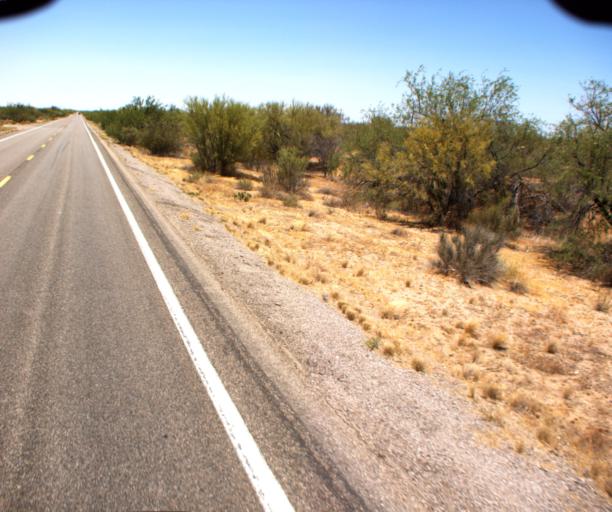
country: US
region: Arizona
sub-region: Pima County
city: Catalina
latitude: 32.7526
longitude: -111.1360
